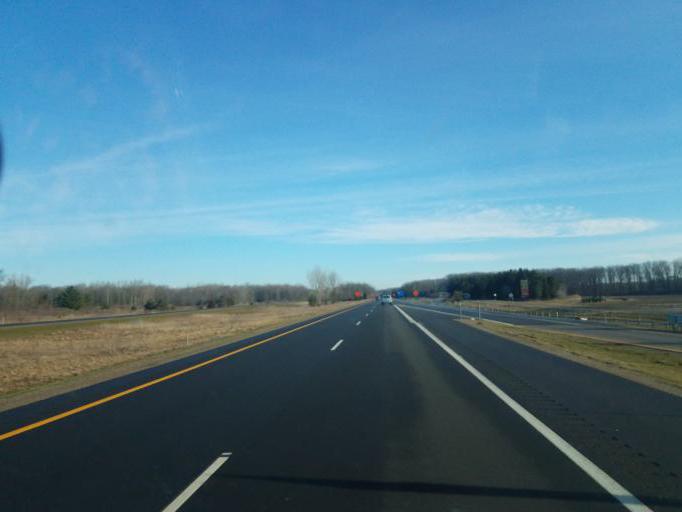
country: US
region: Michigan
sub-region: Gratiot County
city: Saint Louis
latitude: 43.3554
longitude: -84.6012
